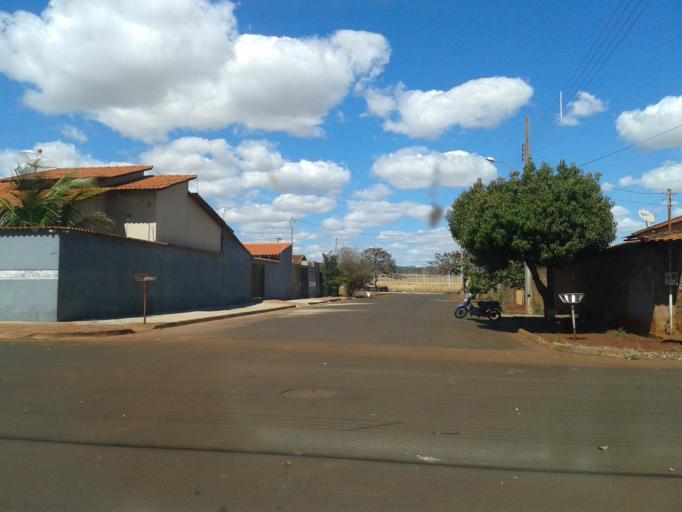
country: BR
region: Minas Gerais
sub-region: Centralina
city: Centralina
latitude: -18.5937
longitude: -49.1996
